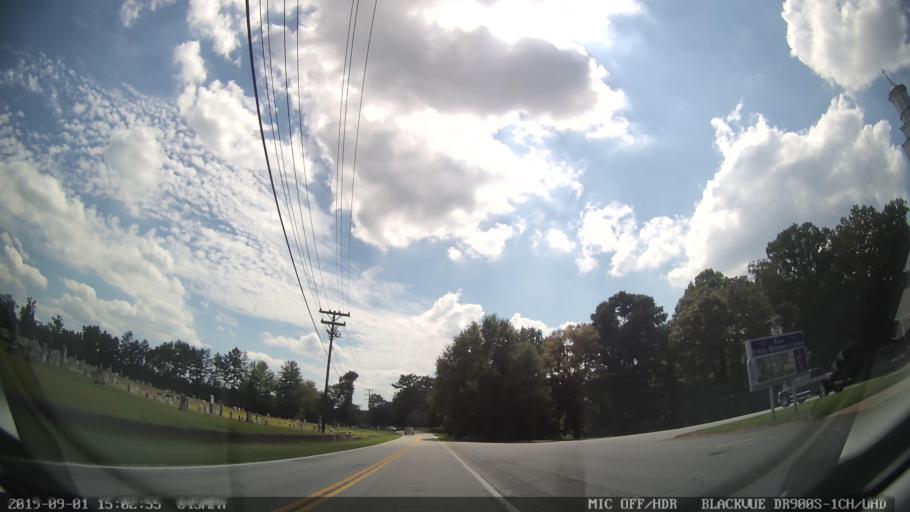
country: US
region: South Carolina
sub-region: Greenville County
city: Greer
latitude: 34.9692
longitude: -82.2009
